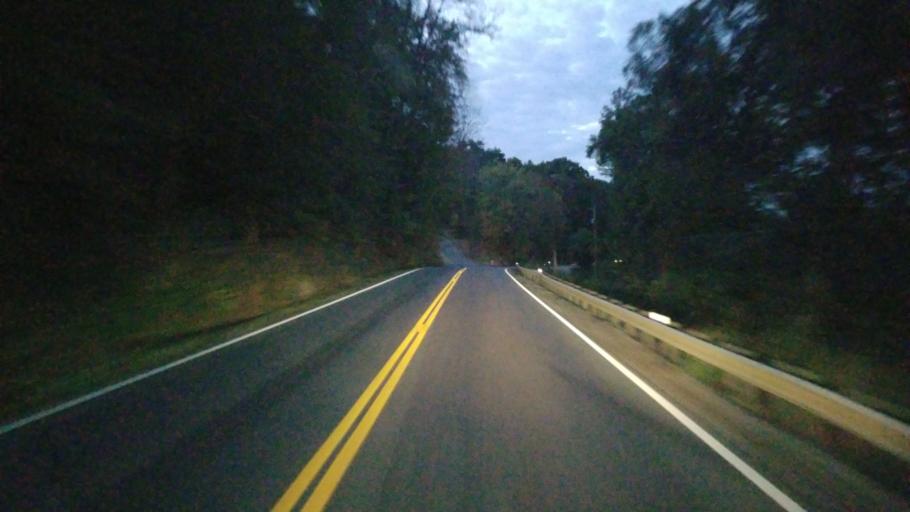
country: US
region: Ohio
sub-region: Scioto County
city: Rosemount
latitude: 38.8263
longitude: -83.0191
